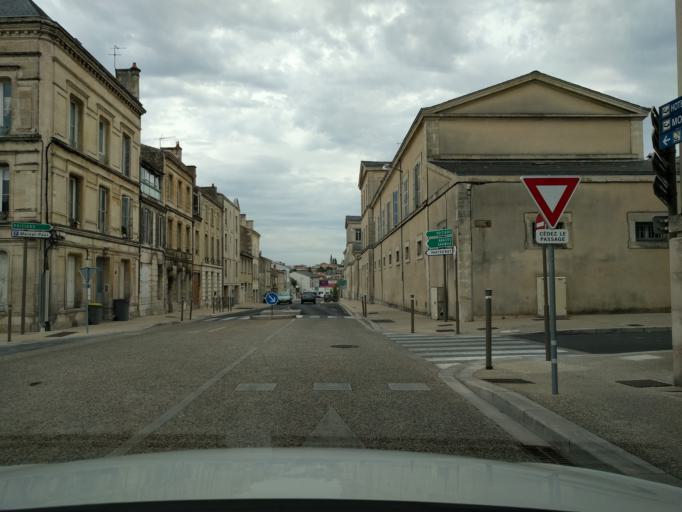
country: FR
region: Poitou-Charentes
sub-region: Departement des Deux-Sevres
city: Niort
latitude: 46.3230
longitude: -0.4562
